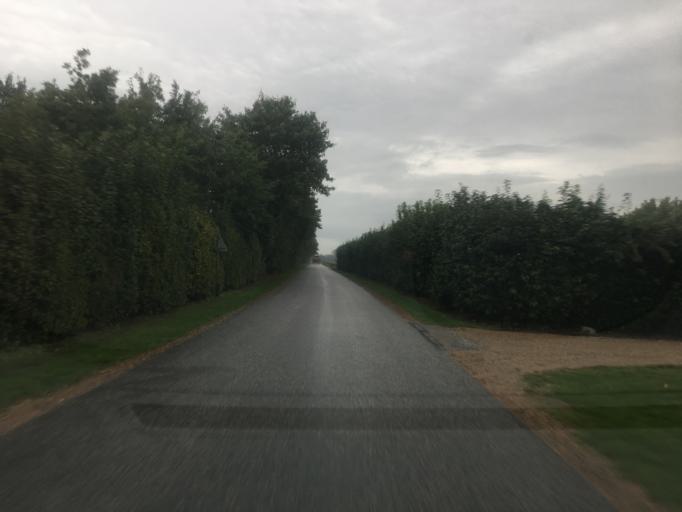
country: DK
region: South Denmark
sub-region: Tonder Kommune
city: Logumkloster
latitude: 55.0210
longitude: 9.0354
